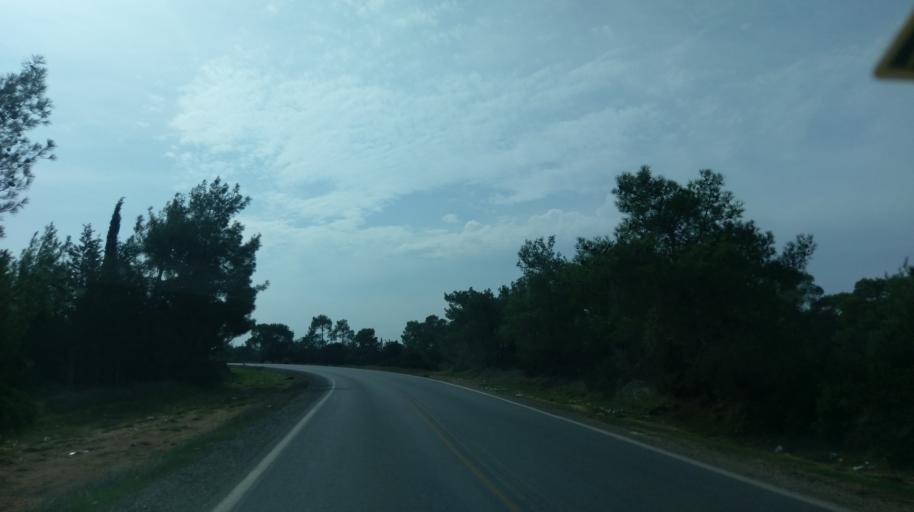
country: CY
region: Lefkosia
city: Morfou
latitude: 35.2898
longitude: 33.0413
